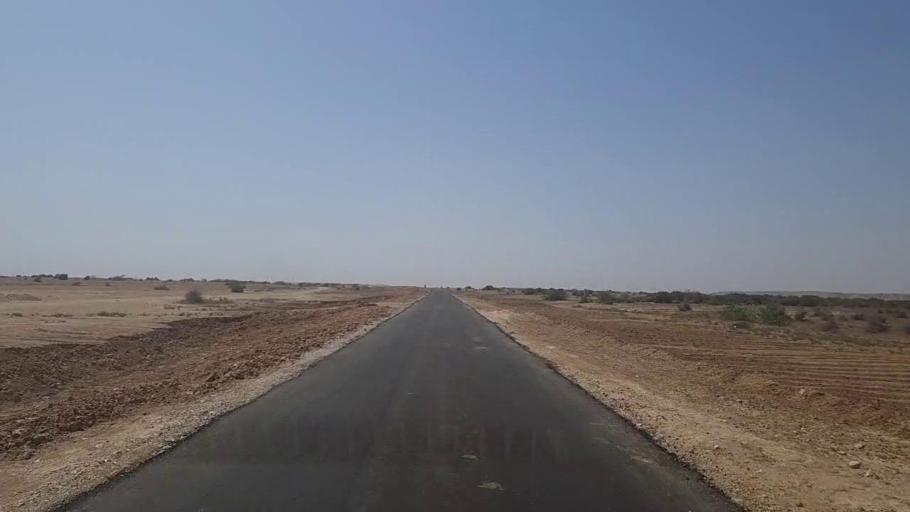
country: PK
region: Sindh
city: Kotri
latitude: 25.1489
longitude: 68.2112
